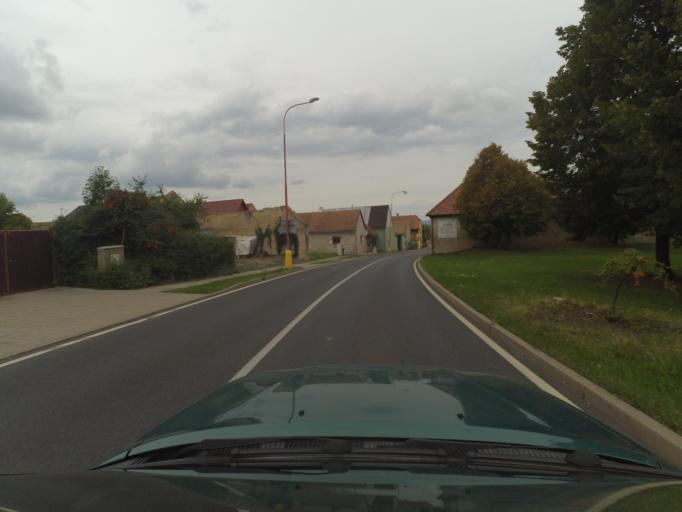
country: CZ
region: Ustecky
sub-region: Okres Louny
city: Louny
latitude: 50.3115
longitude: 13.7993
